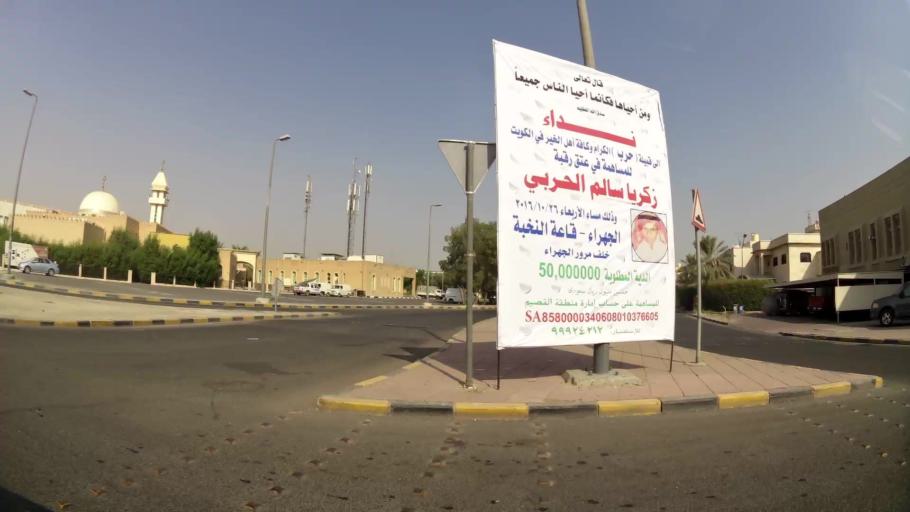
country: KW
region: Al Asimah
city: Ar Rabiyah
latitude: 29.2709
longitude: 47.8769
